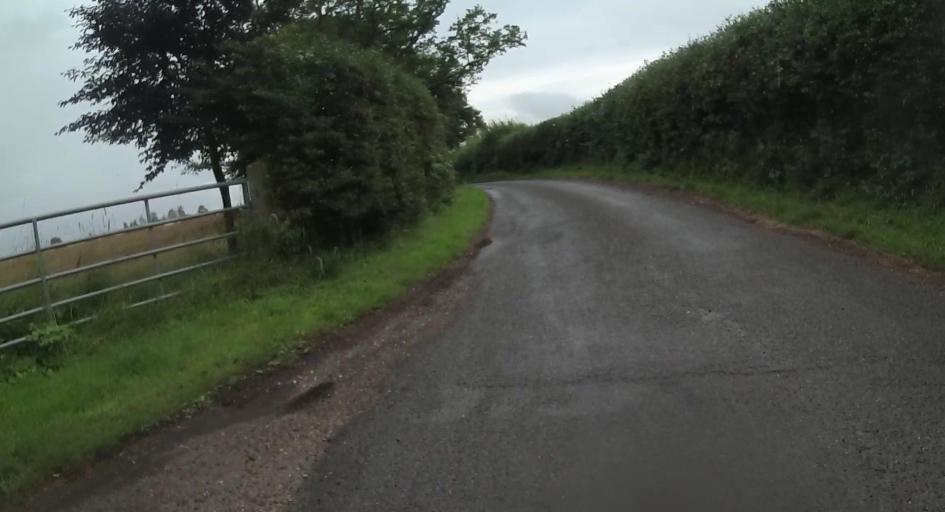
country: GB
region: England
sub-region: Hampshire
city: Highclere
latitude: 51.2742
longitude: -1.3579
